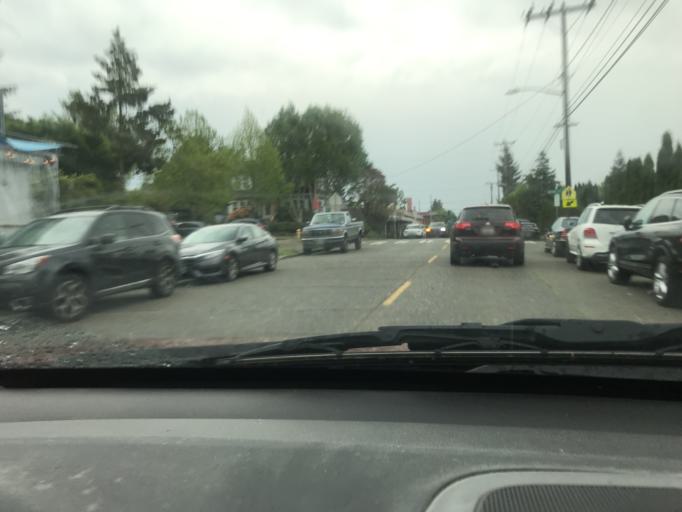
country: US
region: Washington
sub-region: King County
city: Seattle
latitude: 47.6685
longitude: -122.2924
